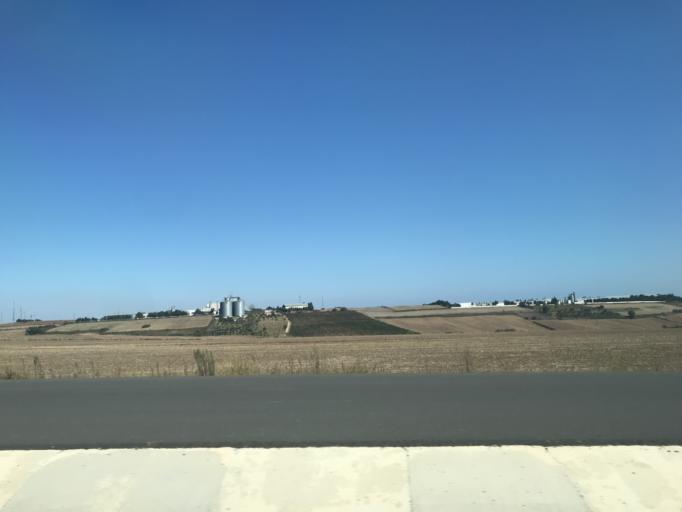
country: TR
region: Tekirdag
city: Kumbag
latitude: 40.9378
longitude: 27.4352
